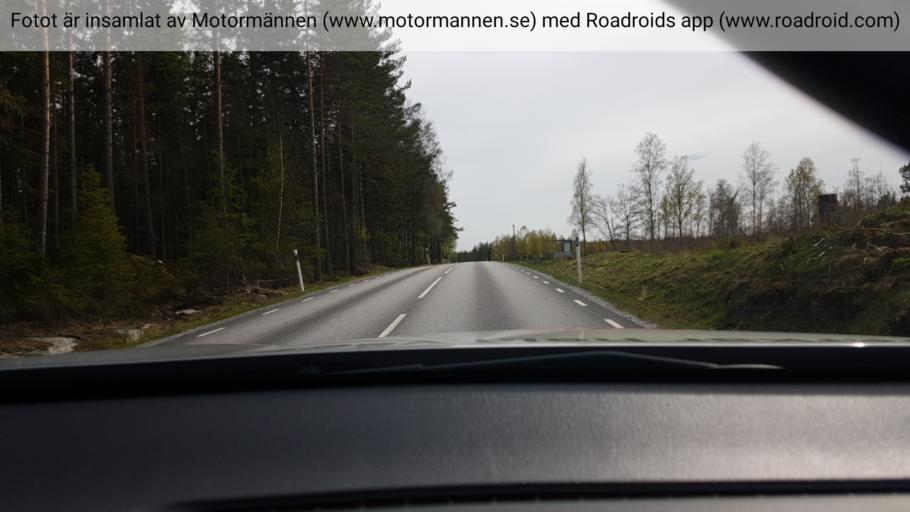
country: SE
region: Stockholm
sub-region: Vallentuna Kommun
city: Vallentuna
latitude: 59.6440
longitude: 18.0216
